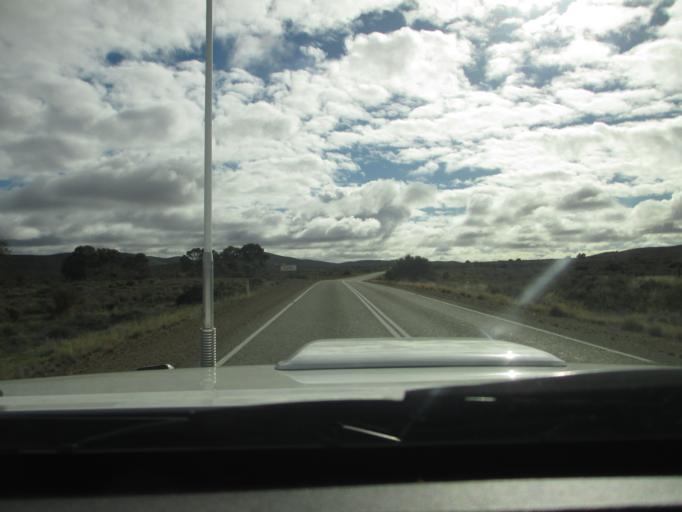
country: AU
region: South Australia
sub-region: Flinders Ranges
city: Quorn
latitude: -32.2326
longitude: 138.5142
